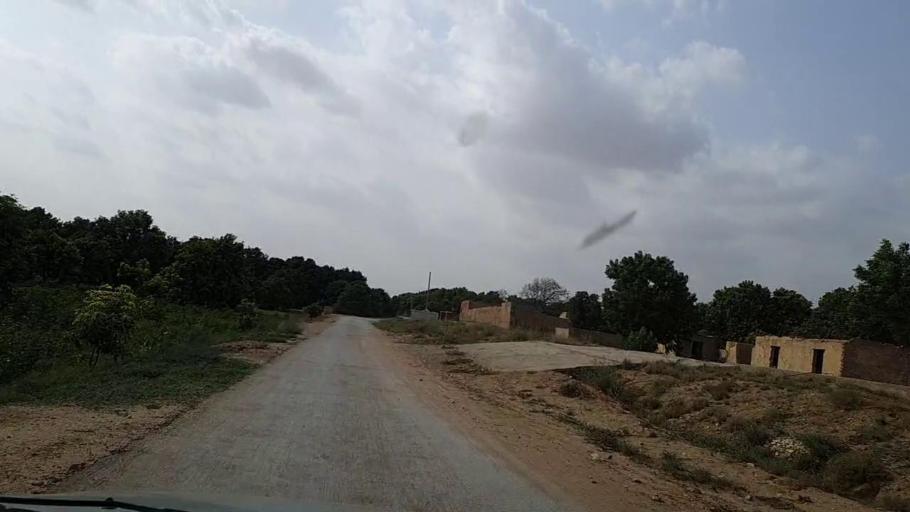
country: PK
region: Sindh
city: Kotri
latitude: 25.2483
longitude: 68.2601
